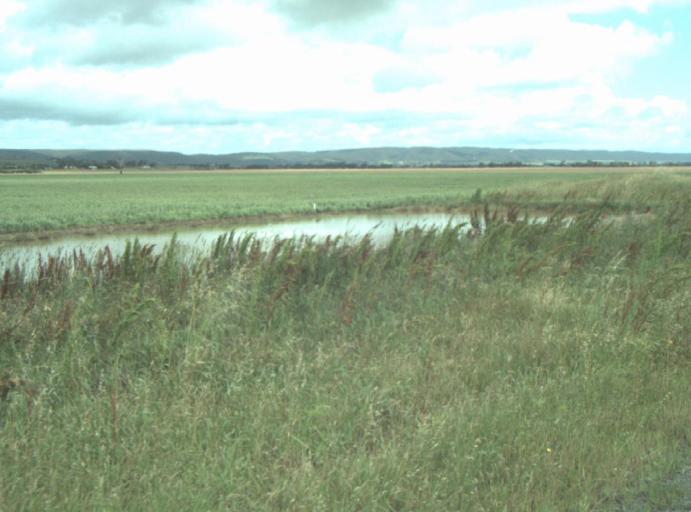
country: AU
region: Victoria
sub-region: Greater Geelong
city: Lara
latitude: -37.8846
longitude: 144.3502
